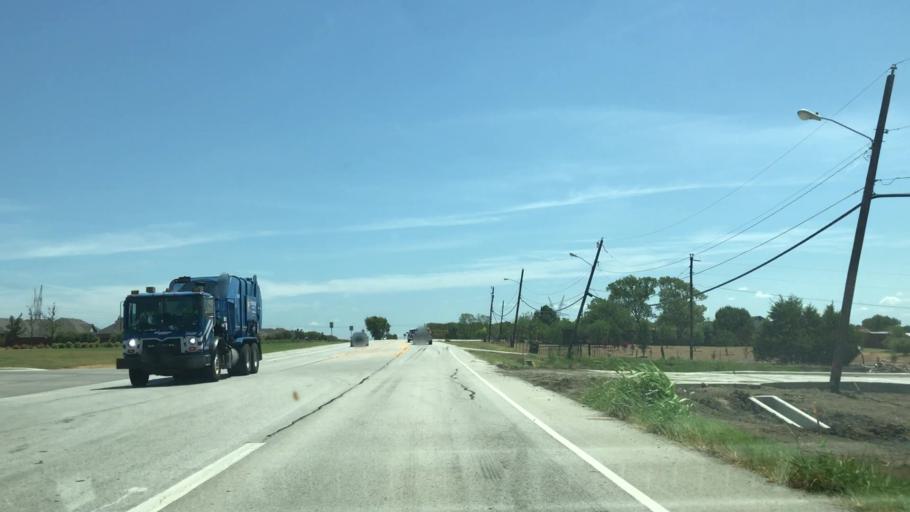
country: US
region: Texas
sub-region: Collin County
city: Saint Paul
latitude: 33.0515
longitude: -96.5539
